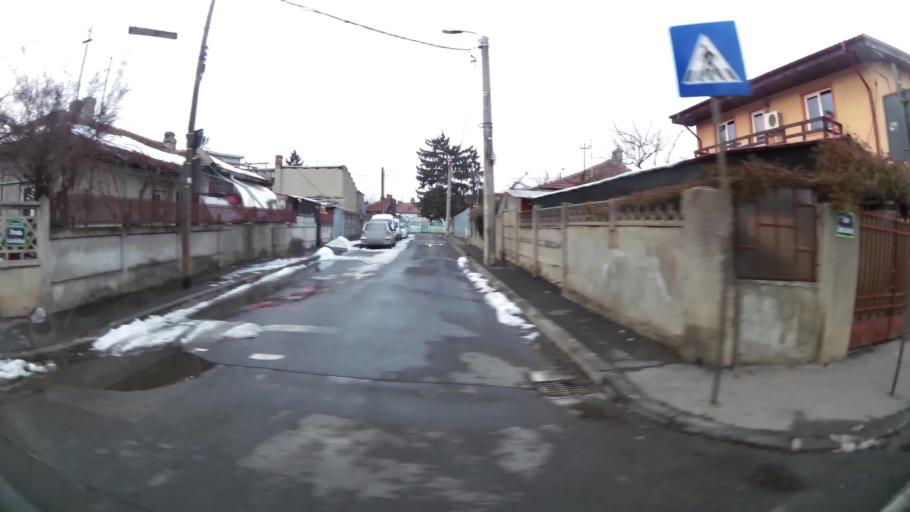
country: RO
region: Ilfov
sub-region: Comuna Fundeni-Dobroesti
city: Fundeni
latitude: 44.4681
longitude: 26.1512
